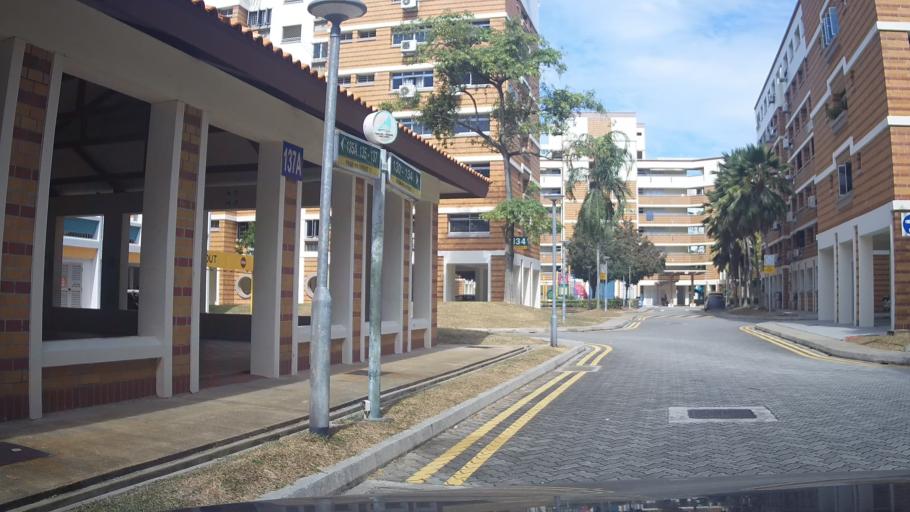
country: SG
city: Singapore
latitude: 1.3650
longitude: 103.9570
